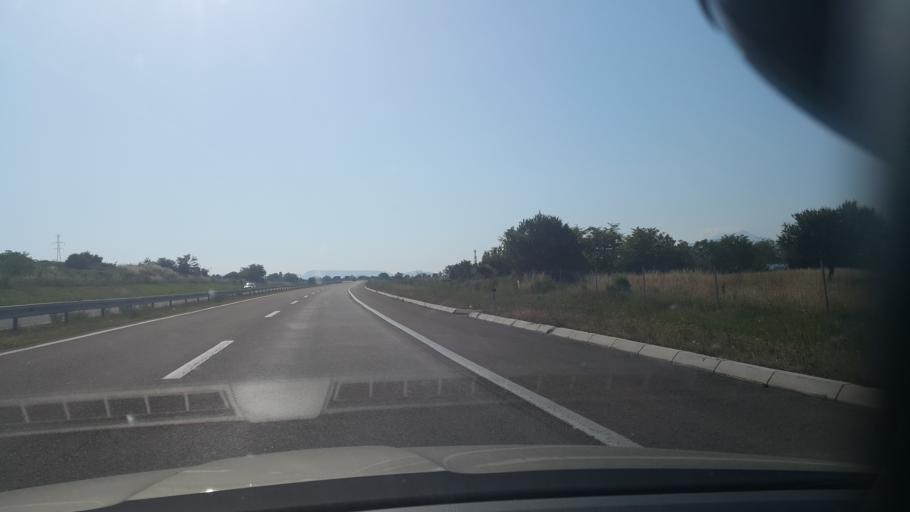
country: RS
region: Central Serbia
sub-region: Nisavski Okrug
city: Nis
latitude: 43.3422
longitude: 21.9001
